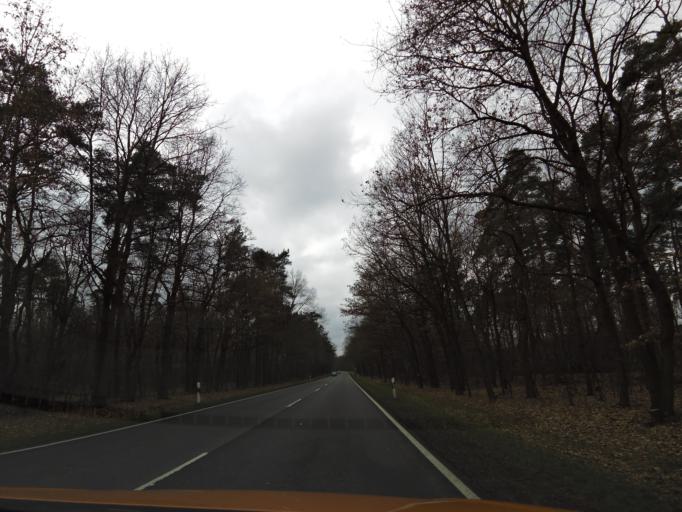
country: DE
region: Brandenburg
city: Nennhausen
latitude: 52.6192
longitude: 12.4396
